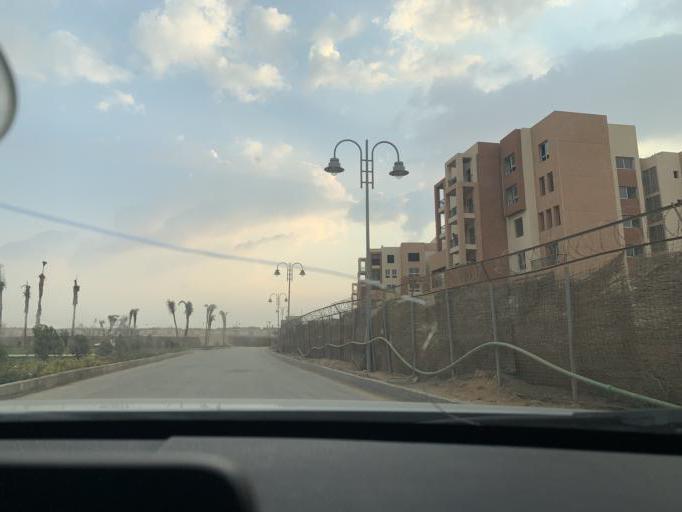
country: EG
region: Muhafazat al Qalyubiyah
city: Al Khankah
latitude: 30.0986
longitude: 31.6512
